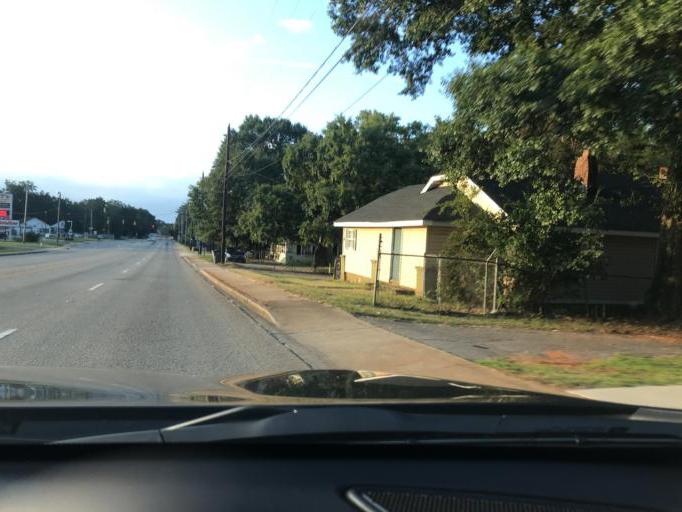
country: US
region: South Carolina
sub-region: Greenville County
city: Welcome
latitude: 34.8255
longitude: -82.4327
